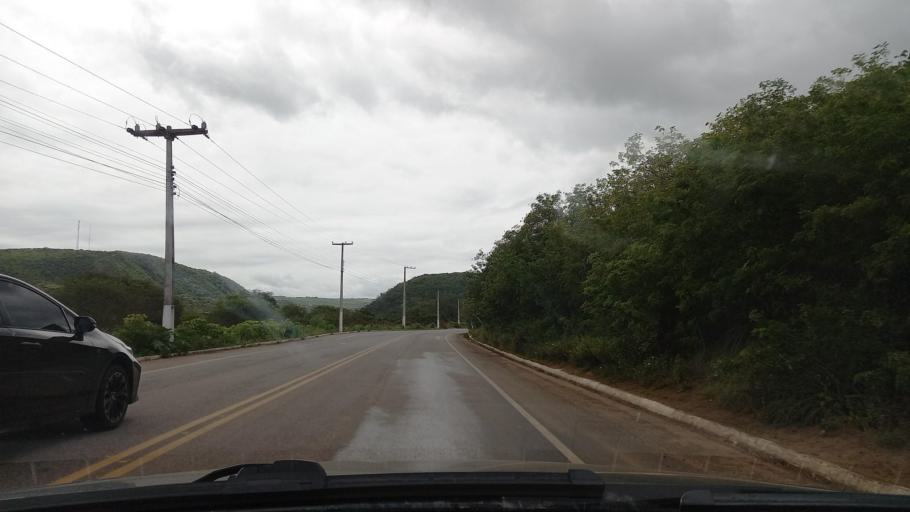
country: BR
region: Sergipe
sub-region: Caninde De Sao Francisco
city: Caninde de Sao Francisco
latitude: -9.6419
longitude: -37.7778
